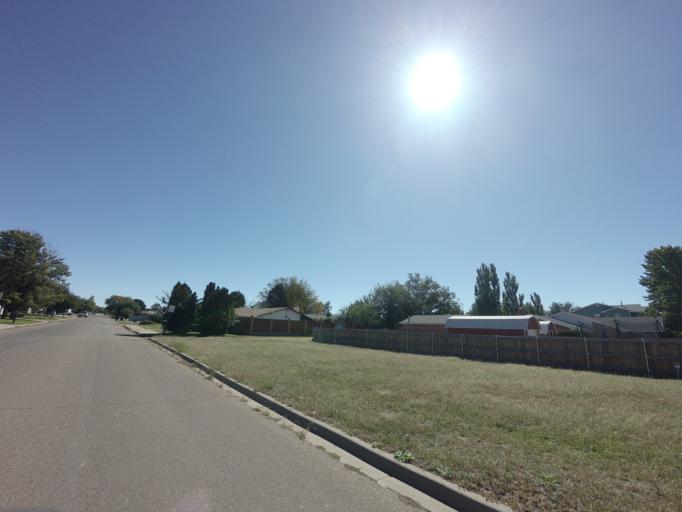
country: US
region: New Mexico
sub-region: Curry County
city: Clovis
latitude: 34.4262
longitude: -103.1880
